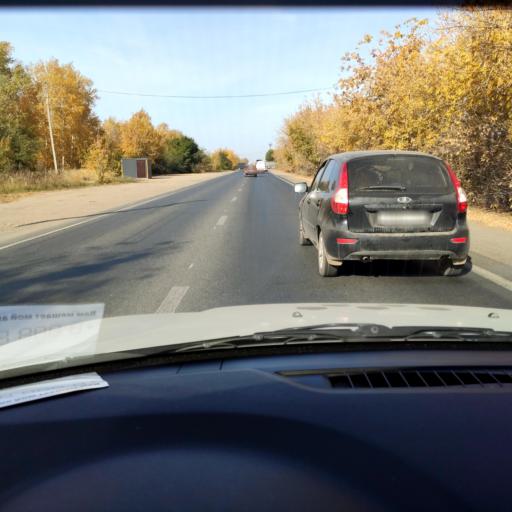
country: RU
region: Samara
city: Tol'yatti
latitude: 53.5586
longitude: 49.3609
